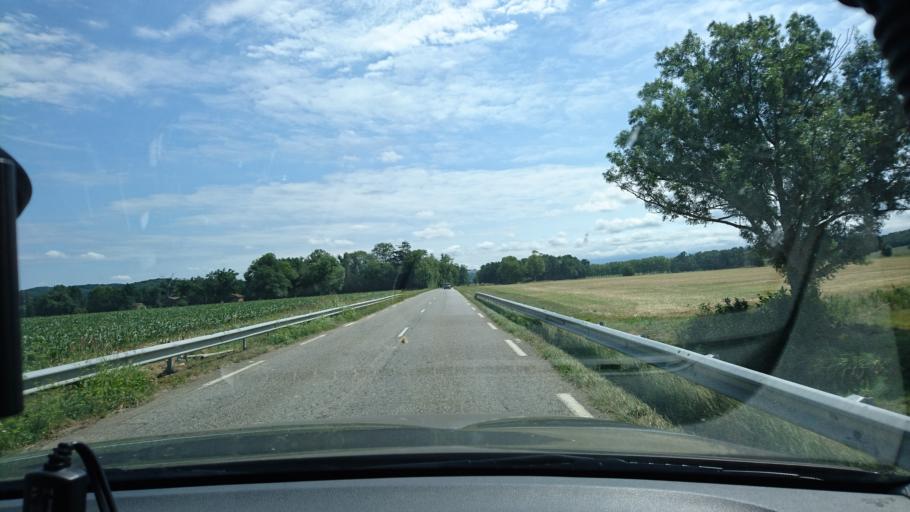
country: FR
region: Midi-Pyrenees
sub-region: Departement de la Haute-Garonne
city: Gaillac-Toulza
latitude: 43.1615
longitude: 1.4202
